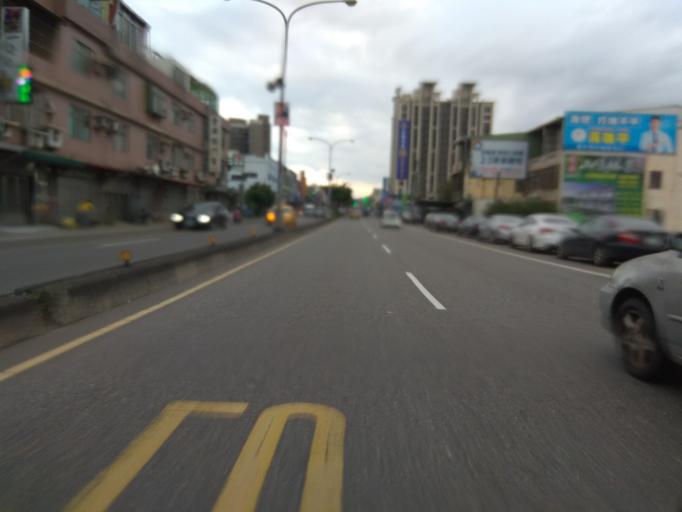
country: TW
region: Taiwan
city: Daxi
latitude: 24.9237
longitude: 121.2120
